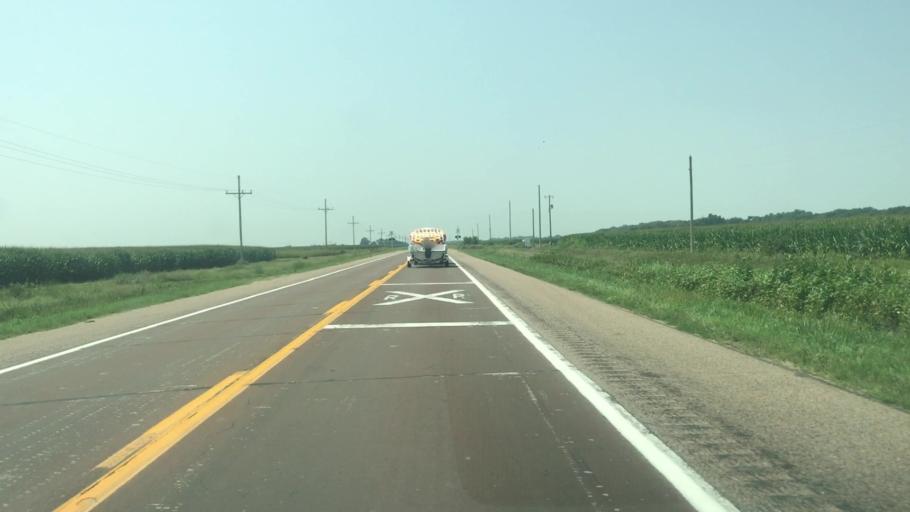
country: US
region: Nebraska
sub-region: Hall County
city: Grand Island
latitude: 40.9675
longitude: -98.4597
